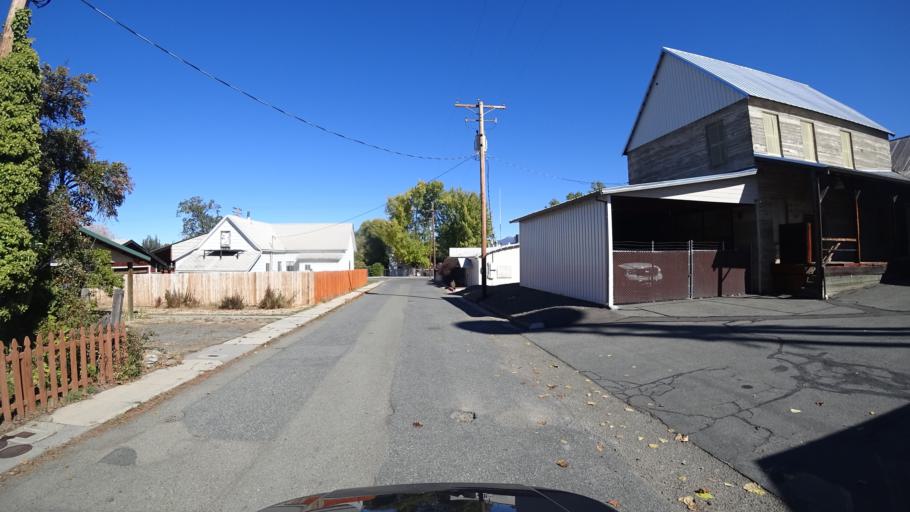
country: US
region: California
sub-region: Siskiyou County
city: Yreka
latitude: 41.4567
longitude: -122.8962
